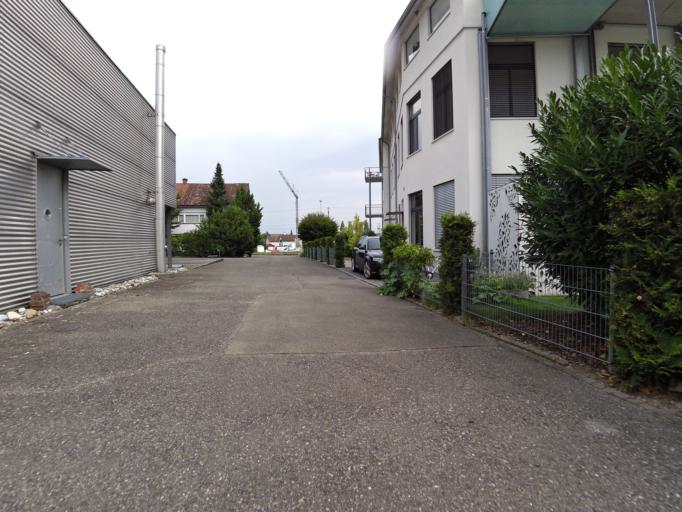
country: CH
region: Thurgau
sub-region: Kreuzlingen District
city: Ermatingen
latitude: 47.6687
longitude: 9.0868
